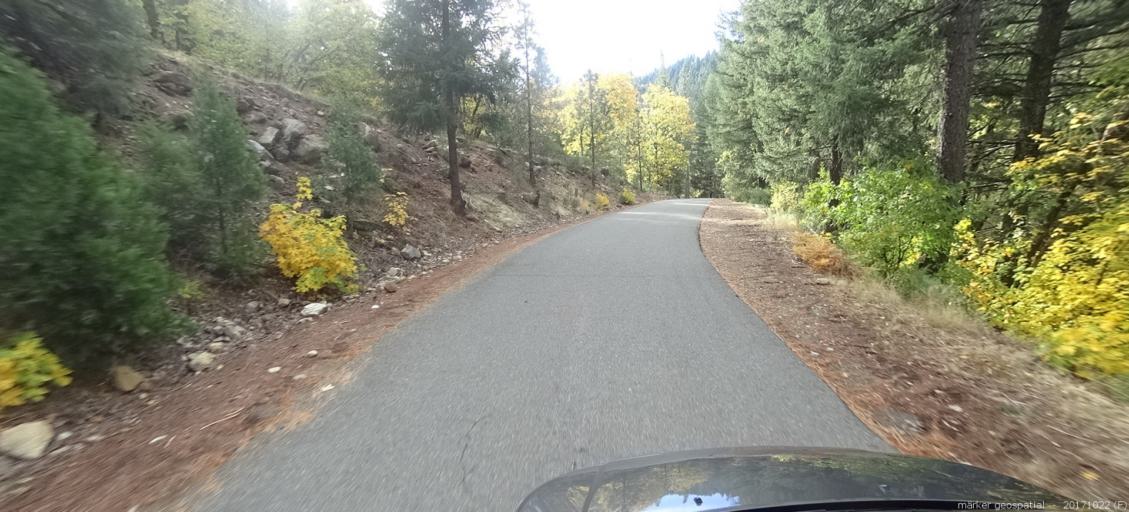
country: US
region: California
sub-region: Siskiyou County
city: Dunsmuir
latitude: 41.1490
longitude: -122.3323
